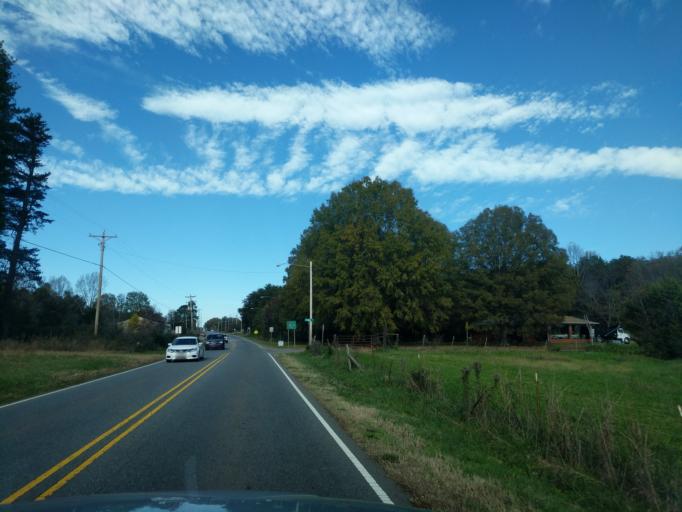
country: US
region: North Carolina
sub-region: Catawba County
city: Newton
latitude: 35.6334
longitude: -81.2671
